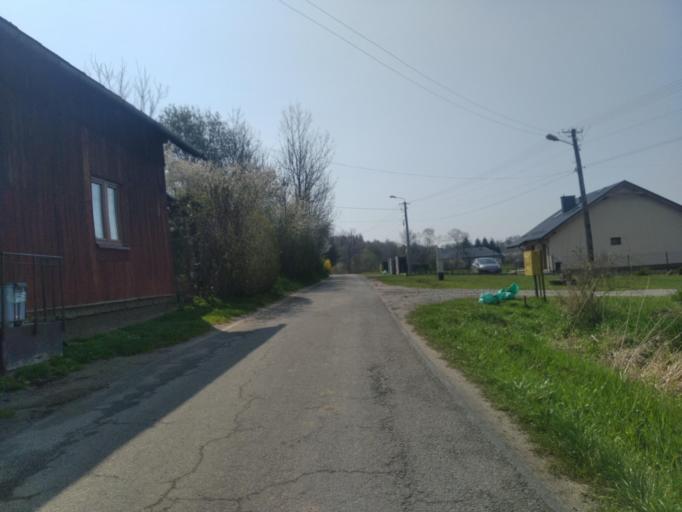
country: PL
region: Subcarpathian Voivodeship
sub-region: Powiat brzozowski
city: Brzozow
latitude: 49.6966
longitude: 22.0296
